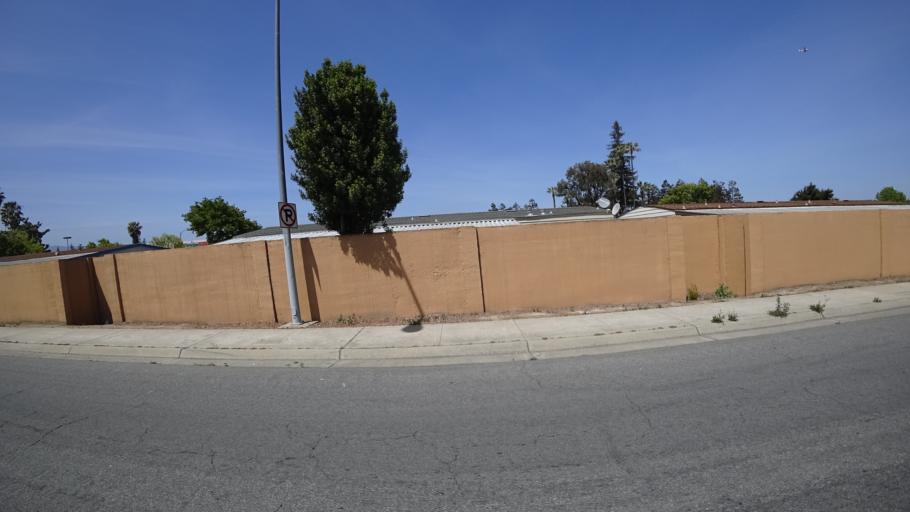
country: US
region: California
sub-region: Santa Clara County
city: Seven Trees
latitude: 37.3144
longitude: -121.8081
